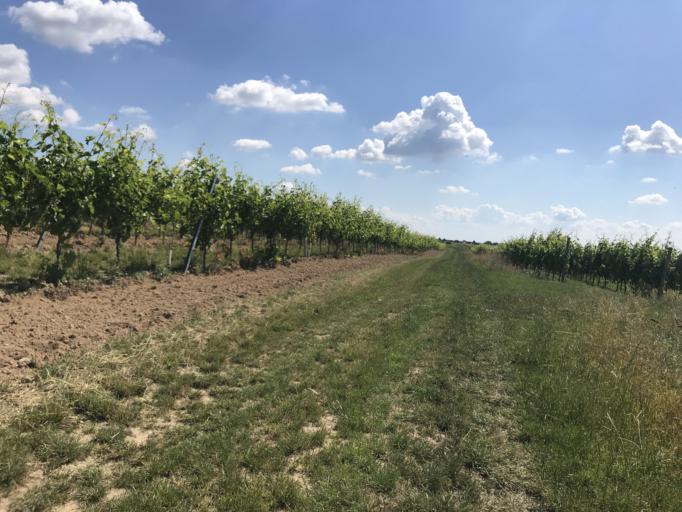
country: DE
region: Rheinland-Pfalz
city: Stadecken-Elsheim
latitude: 49.9284
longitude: 8.1318
